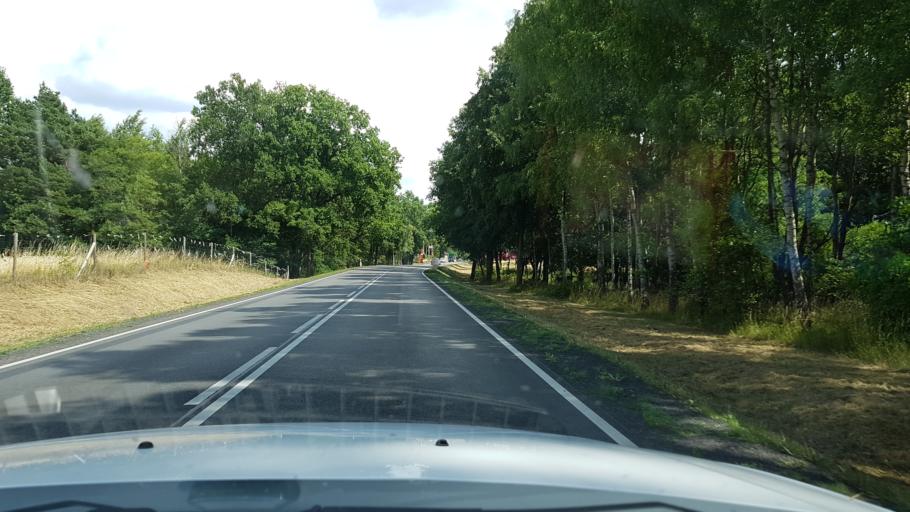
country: PL
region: West Pomeranian Voivodeship
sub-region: Powiat walecki
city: Walcz
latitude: 53.3076
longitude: 16.3929
